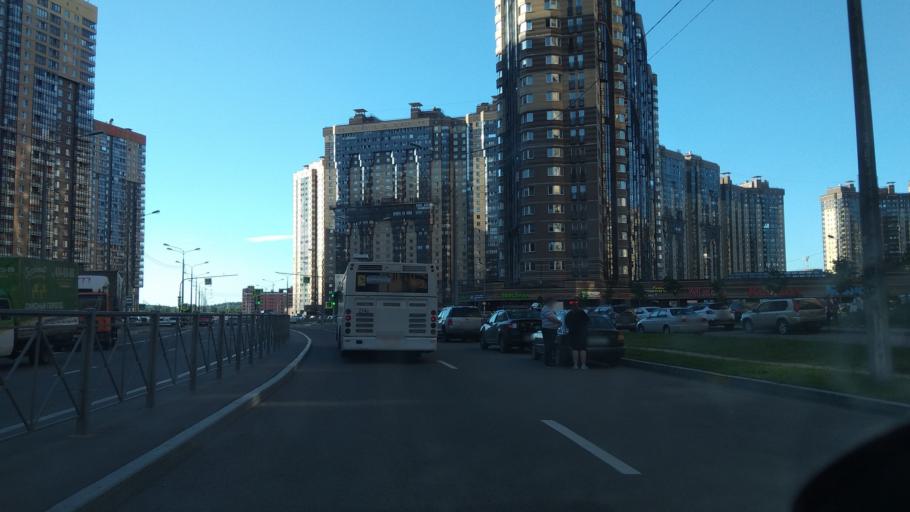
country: RU
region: Leningrad
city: Parnas
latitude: 60.0784
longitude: 30.3436
